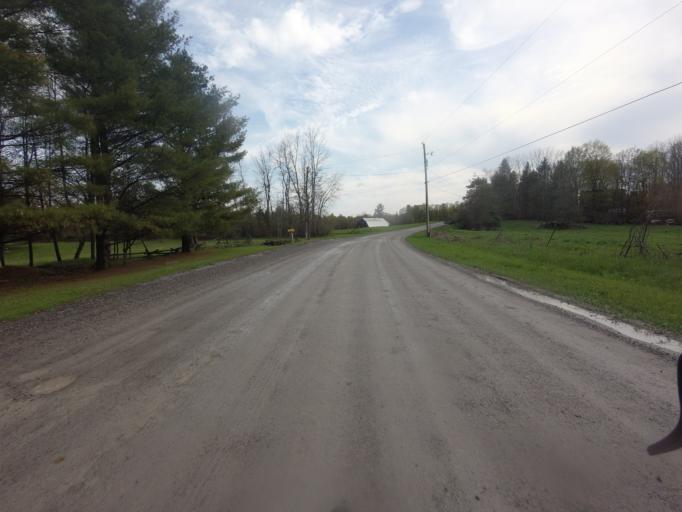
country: CA
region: Ontario
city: Carleton Place
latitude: 45.2020
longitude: -76.3232
